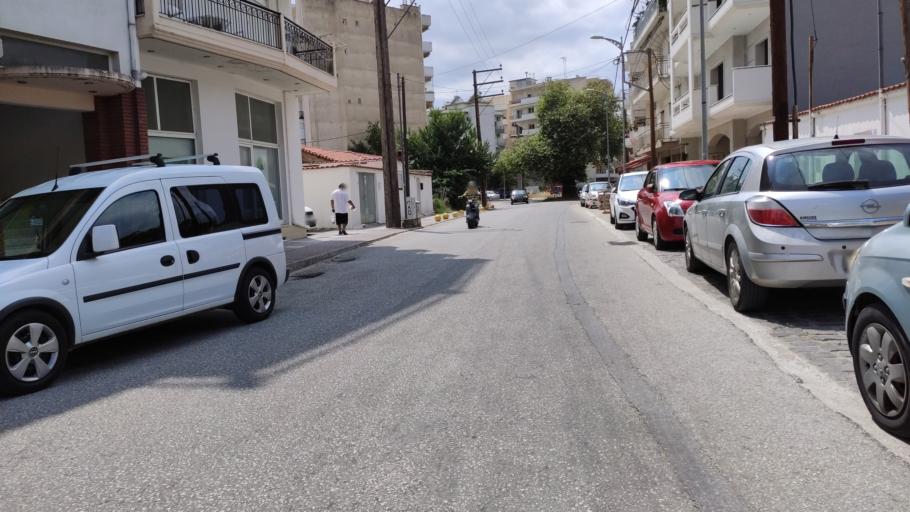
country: GR
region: East Macedonia and Thrace
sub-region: Nomos Rodopis
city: Komotini
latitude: 41.1226
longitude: 25.4039
